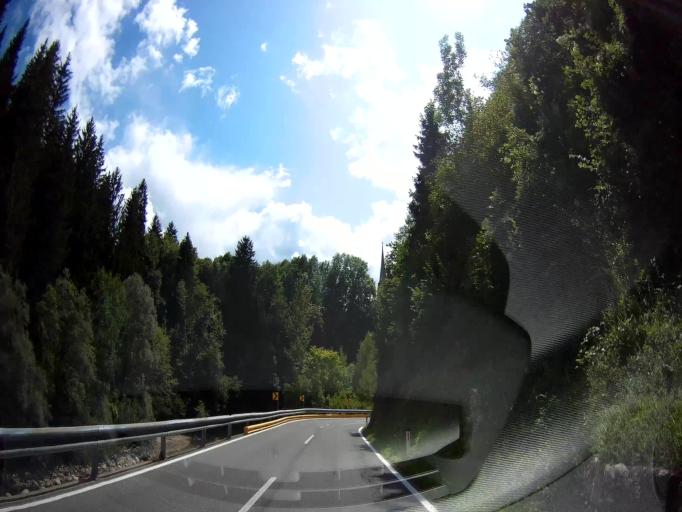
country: AT
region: Carinthia
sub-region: Politischer Bezirk Spittal an der Drau
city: Seeboden
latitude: 46.8343
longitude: 13.4941
